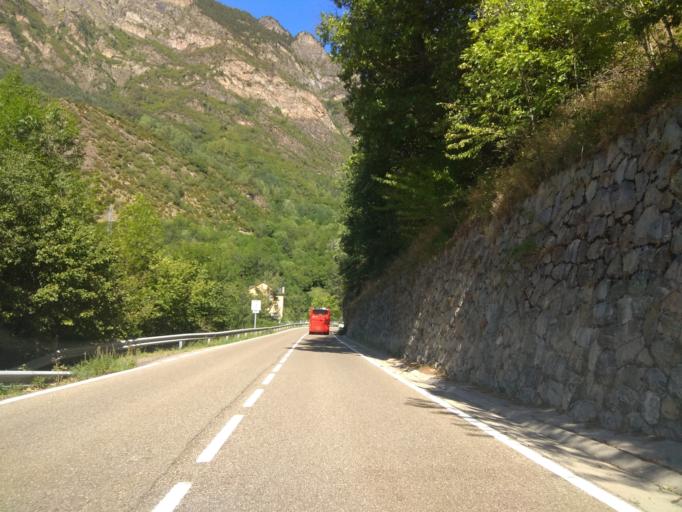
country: ES
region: Catalonia
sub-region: Provincia de Lleida
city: Vielha
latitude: 42.5299
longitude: 0.8337
